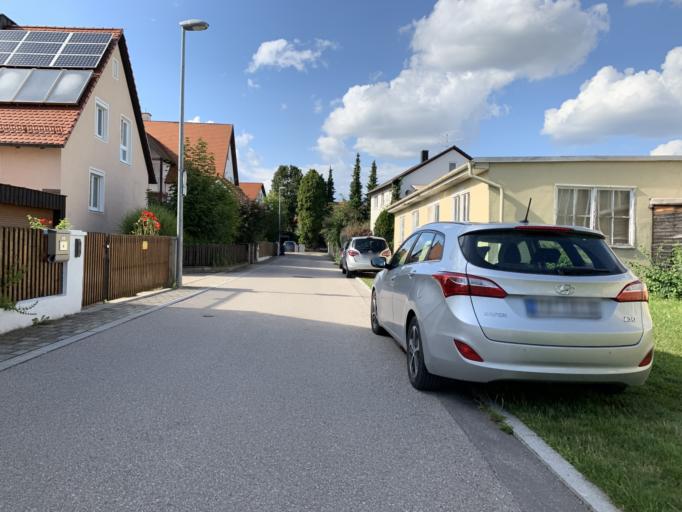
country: DE
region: Bavaria
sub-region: Upper Bavaria
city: Freising
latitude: 48.3967
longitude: 11.7671
